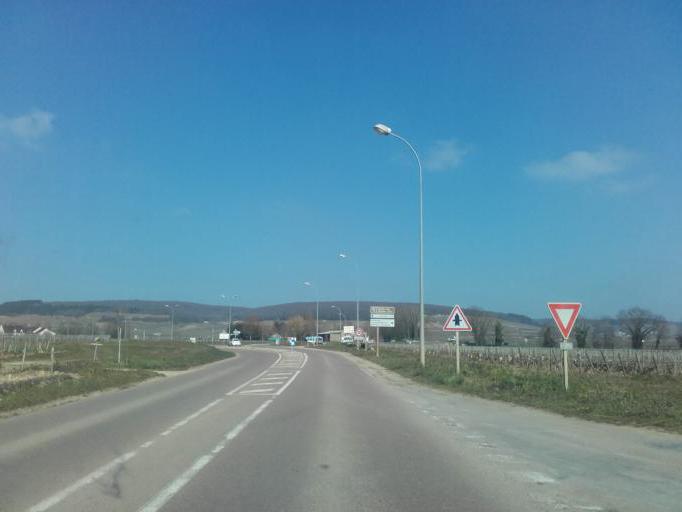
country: FR
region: Bourgogne
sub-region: Departement de la Cote-d'Or
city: Beaune
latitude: 47.0519
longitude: 4.8393
